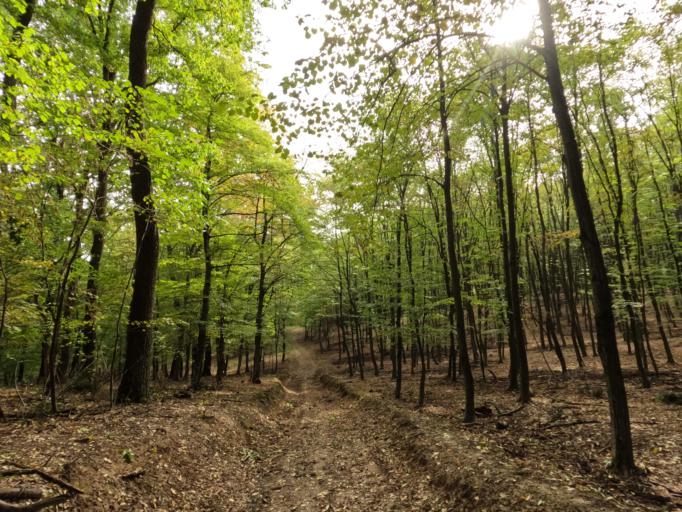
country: HU
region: Tolna
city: Szentgalpuszta
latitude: 46.3149
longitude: 18.6438
